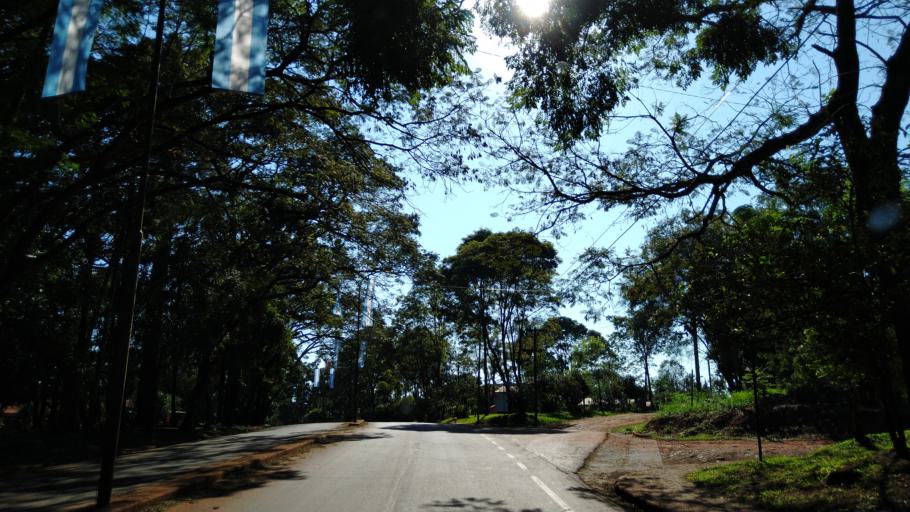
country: AR
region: Misiones
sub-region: Departamento de Montecarlo
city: Montecarlo
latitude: -26.5698
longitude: -54.7266
